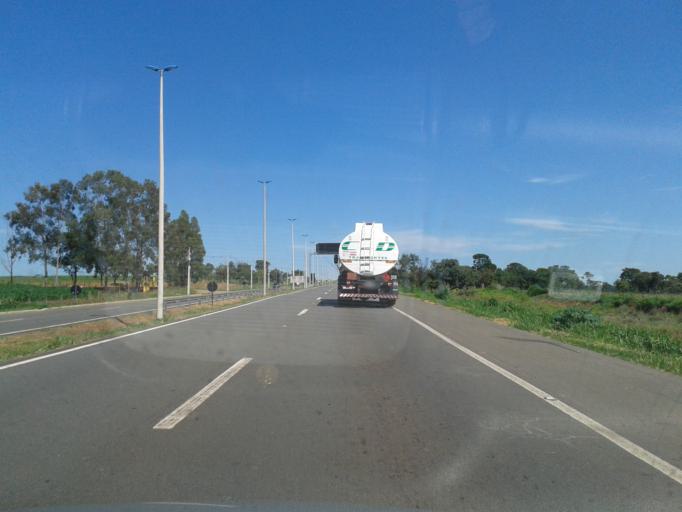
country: BR
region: Goias
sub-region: Bela Vista De Goias
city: Bela Vista de Goias
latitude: -17.0320
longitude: -48.9514
